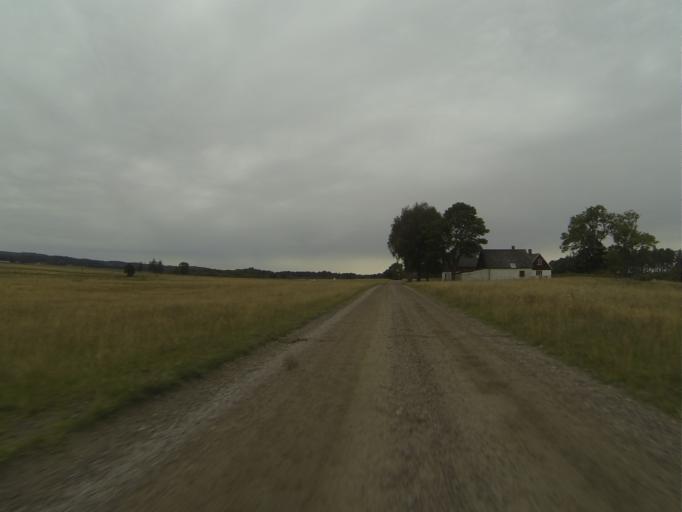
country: SE
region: Skane
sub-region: Lunds Kommun
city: Veberod
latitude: 55.7135
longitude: 13.4273
